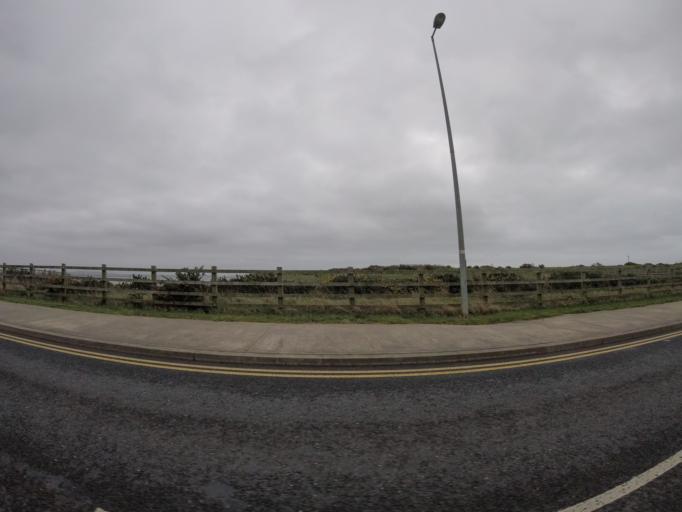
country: IE
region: Munster
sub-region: Waterford
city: Tra Mhor
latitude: 52.1633
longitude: -7.1344
